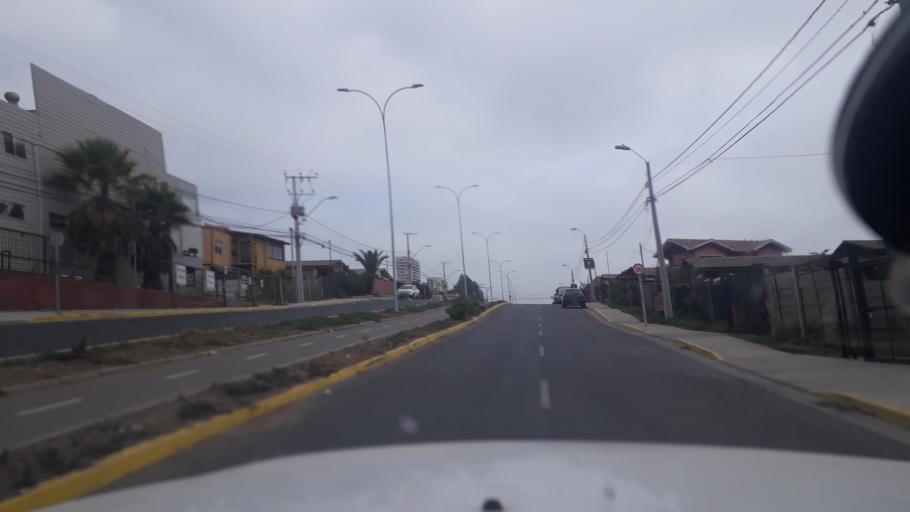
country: CL
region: Valparaiso
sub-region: Provincia de Valparaiso
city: Vina del Mar
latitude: -32.9351
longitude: -71.5279
